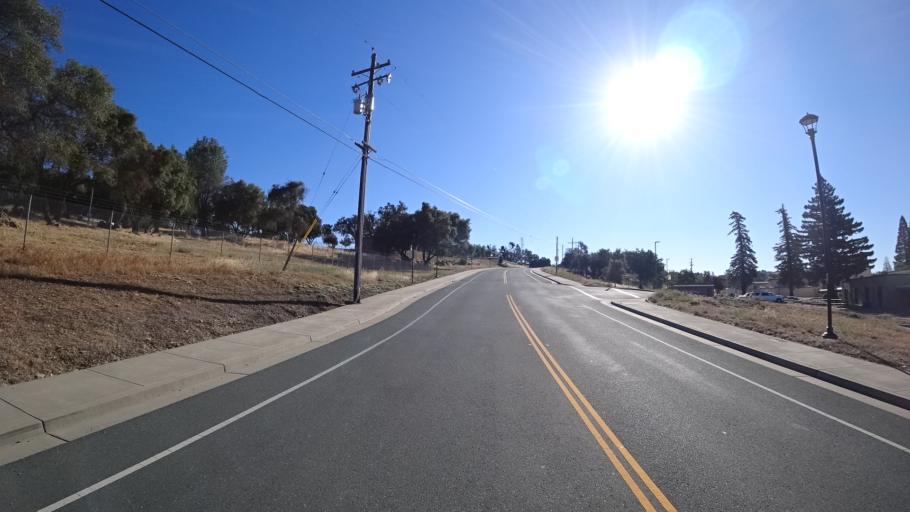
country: US
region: California
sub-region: Calaveras County
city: San Andreas
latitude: 38.1916
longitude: -120.6684
